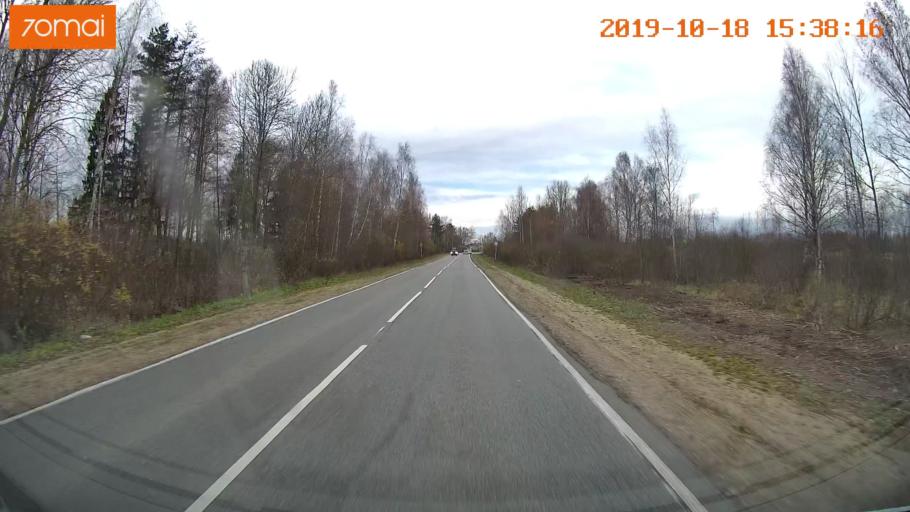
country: RU
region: Vladimir
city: Golovino
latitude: 55.9089
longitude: 40.6082
